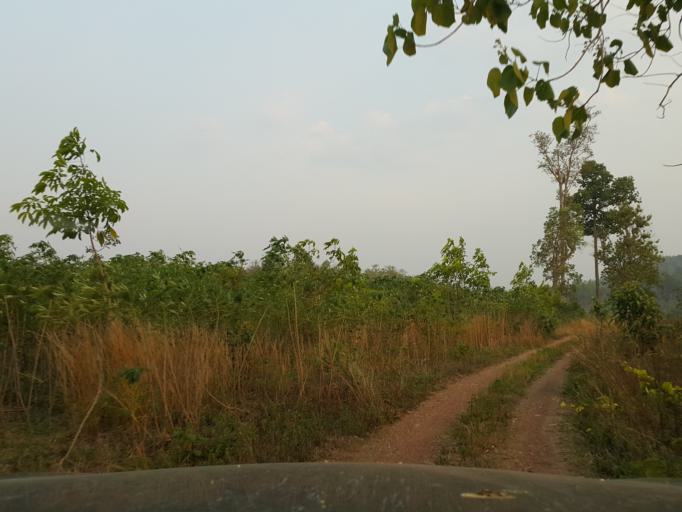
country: TH
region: Lamphun
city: Thung Hua Chang
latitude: 17.9145
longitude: 99.0738
